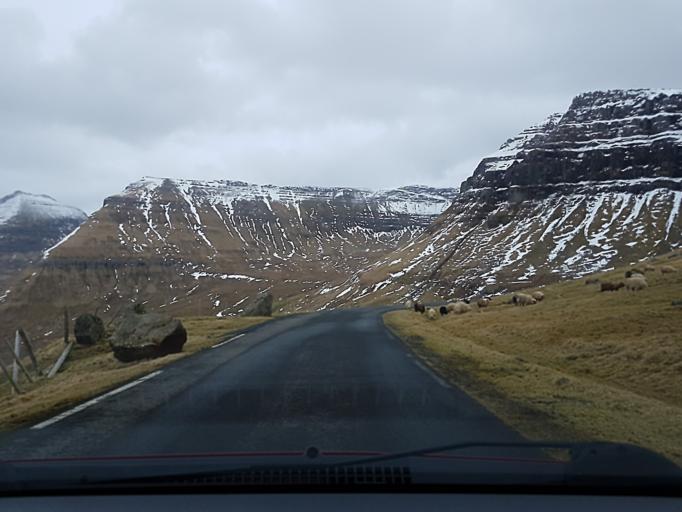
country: FO
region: Streymoy
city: Kollafjordhur
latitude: 62.0143
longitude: -6.9102
